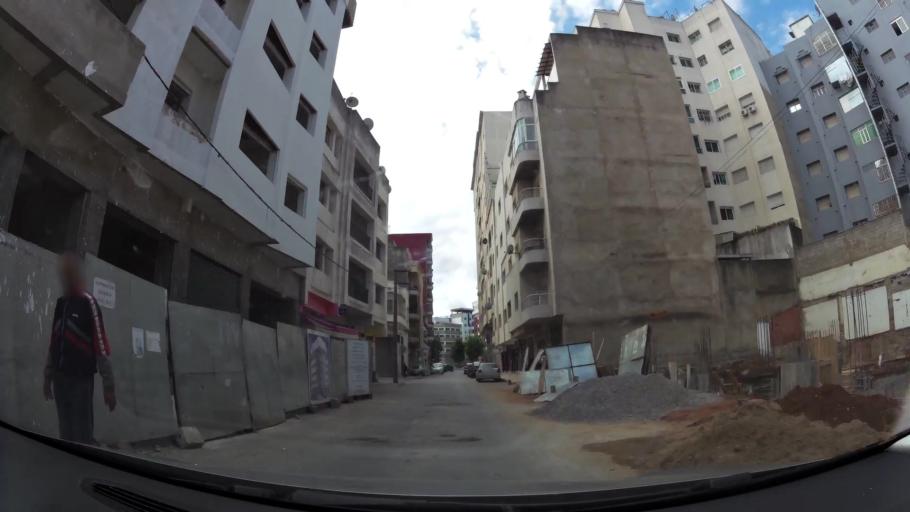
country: MA
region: Gharb-Chrarda-Beni Hssen
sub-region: Kenitra Province
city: Kenitra
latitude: 34.2572
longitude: -6.5871
